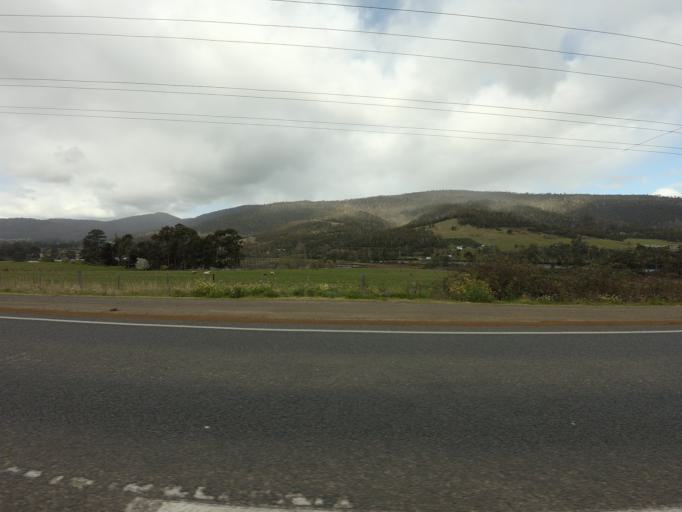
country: AU
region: Tasmania
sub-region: Huon Valley
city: Huonville
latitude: -43.0402
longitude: 147.0451
